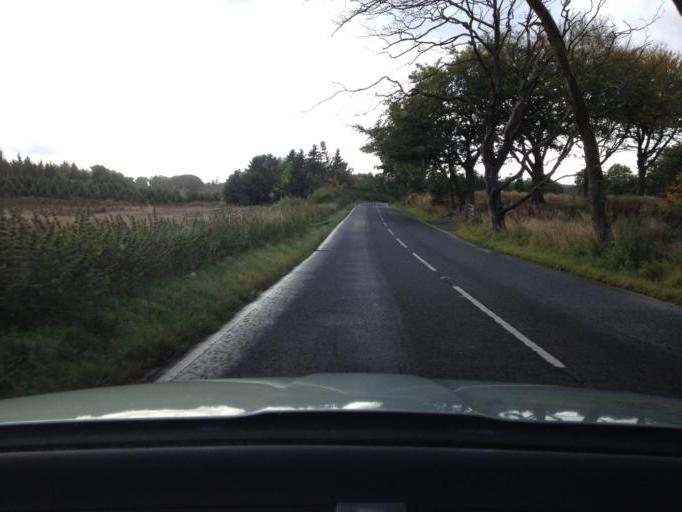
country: GB
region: Scotland
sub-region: West Lothian
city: West Calder
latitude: 55.8293
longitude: -3.5384
